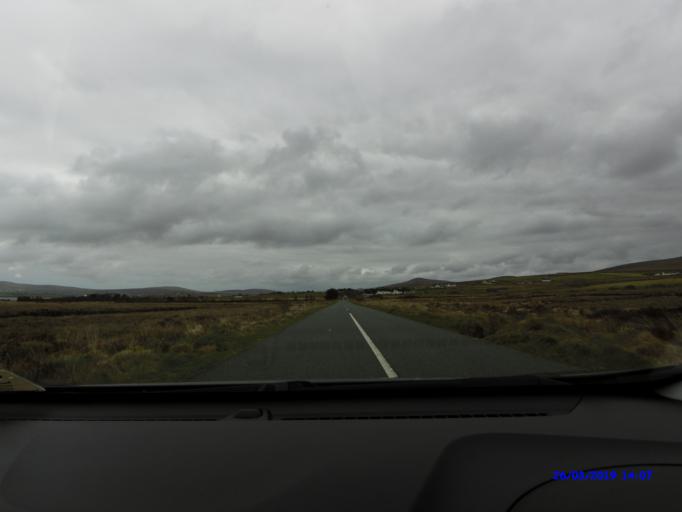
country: IE
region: Connaught
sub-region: Maigh Eo
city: Belmullet
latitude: 54.2084
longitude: -9.9074
